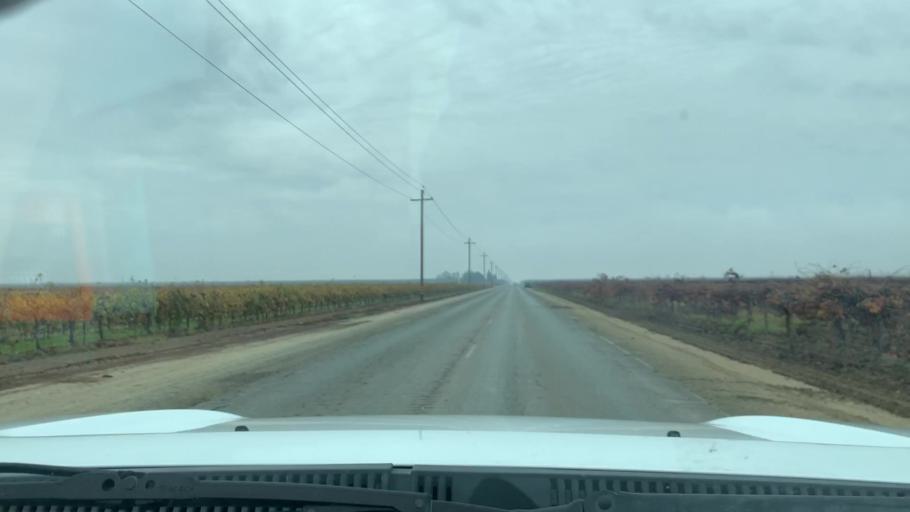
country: US
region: California
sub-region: Kern County
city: Delano
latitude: 35.7611
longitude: -119.3743
